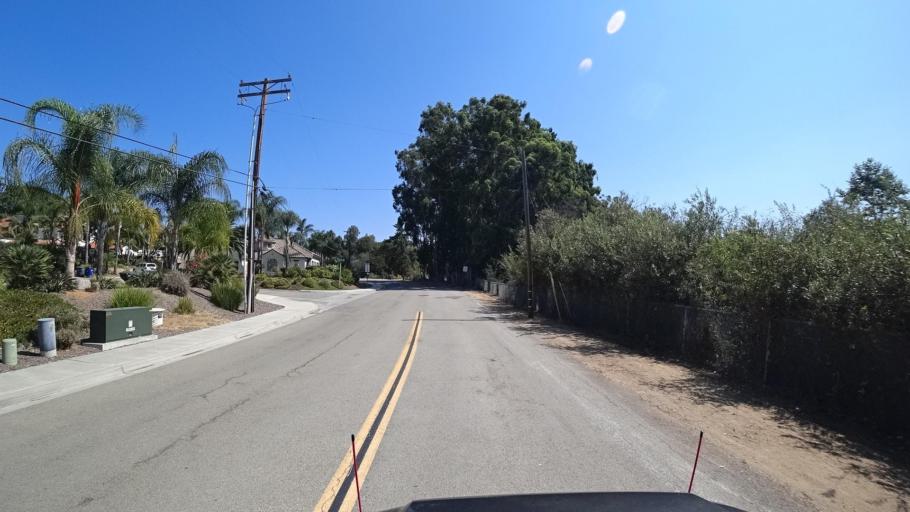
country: US
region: California
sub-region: San Diego County
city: Lake San Marcos
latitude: 33.1575
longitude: -117.2129
